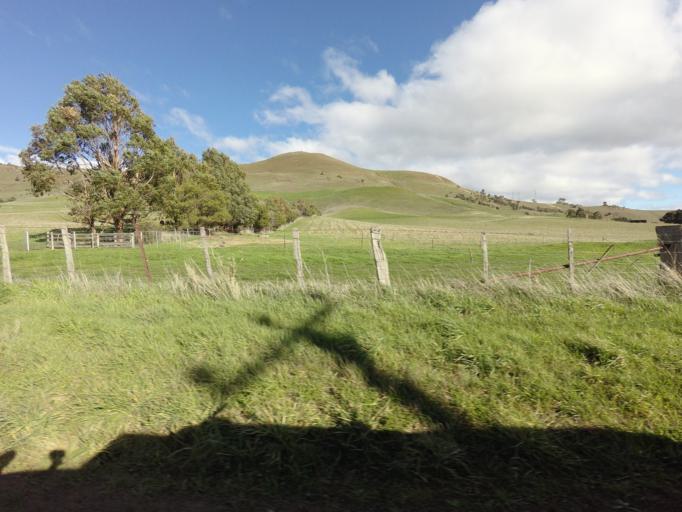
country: AU
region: Tasmania
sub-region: Derwent Valley
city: New Norfolk
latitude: -42.6994
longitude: 146.9812
